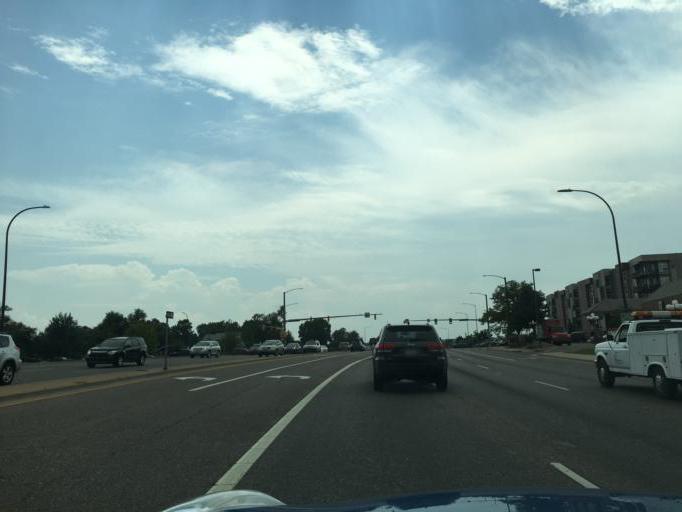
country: US
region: Colorado
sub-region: Jefferson County
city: Arvada
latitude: 39.8032
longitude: -105.0771
